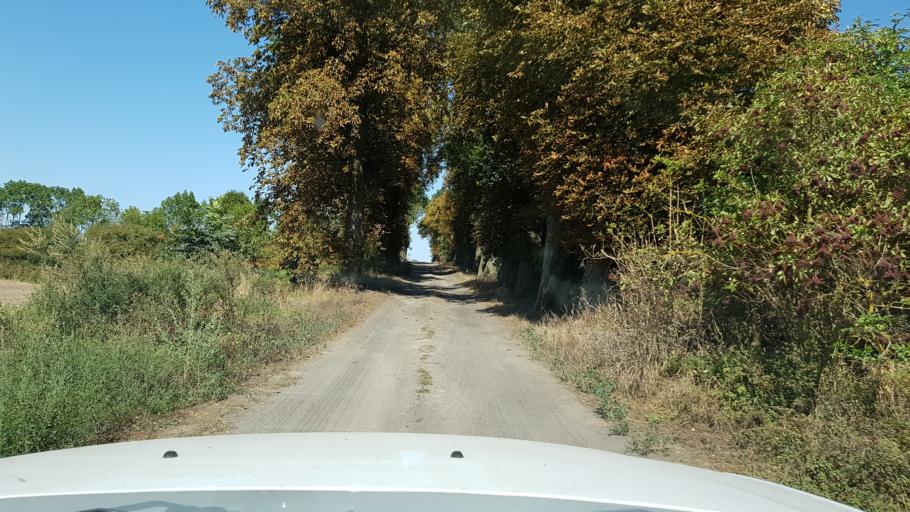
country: PL
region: West Pomeranian Voivodeship
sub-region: Powiat gryfinski
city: Moryn
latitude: 52.8632
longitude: 14.3552
